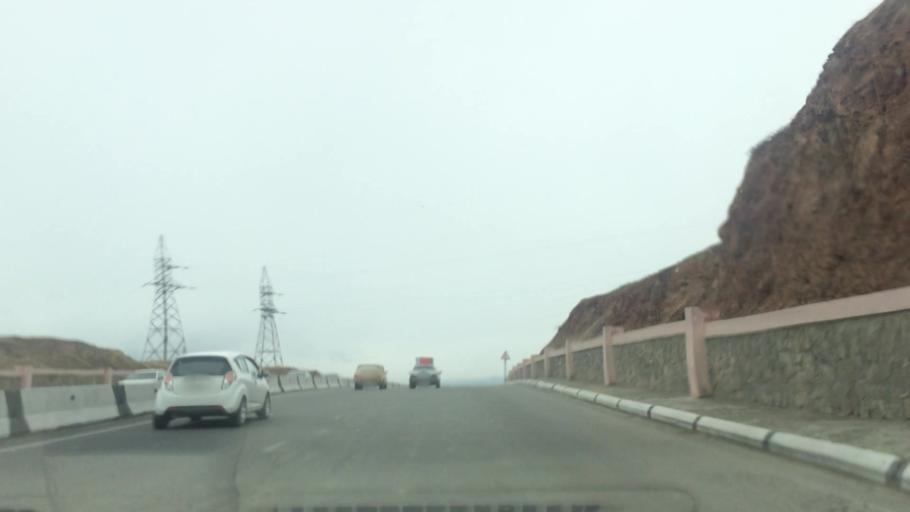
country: UZ
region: Samarqand
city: Jomboy
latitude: 39.6864
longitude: 67.0520
